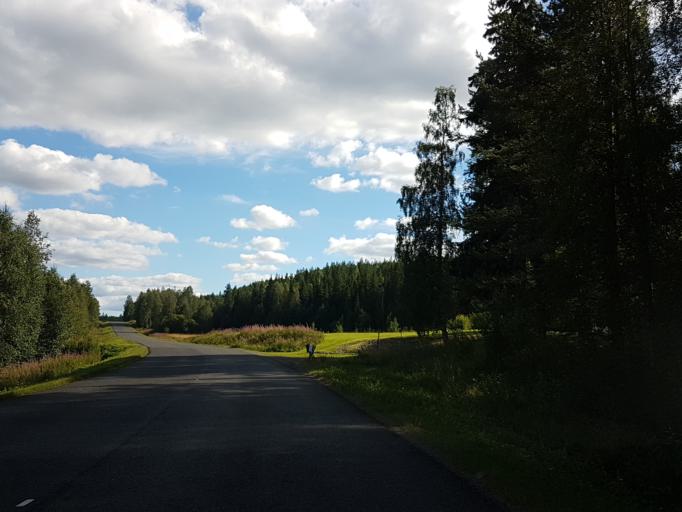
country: SE
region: Vaesterbotten
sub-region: Skelleftea Kommun
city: Burtraesk
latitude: 64.2919
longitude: 20.5233
